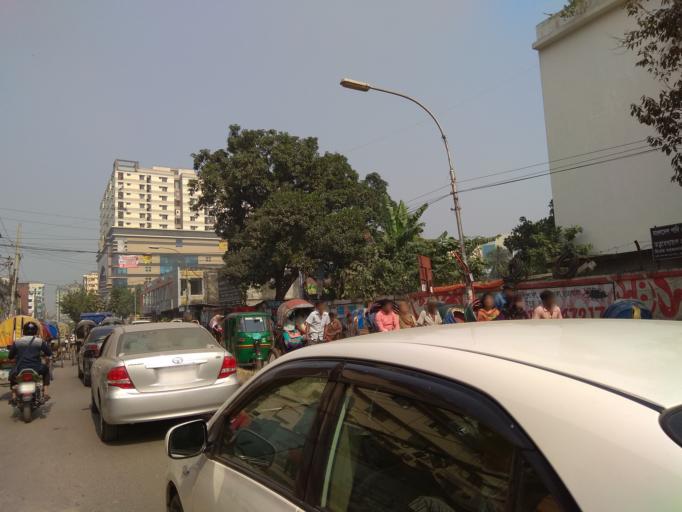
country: BD
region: Dhaka
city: Azimpur
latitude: 23.7530
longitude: 90.3880
